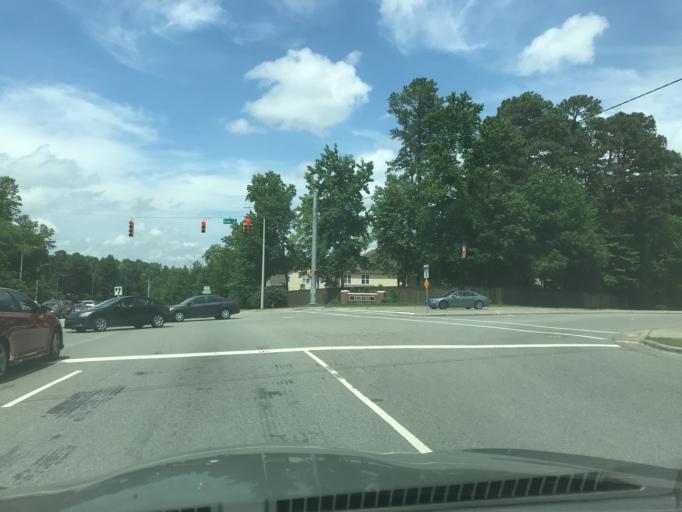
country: US
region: North Carolina
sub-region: Wake County
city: Wake Forest
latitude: 35.9255
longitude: -78.5879
